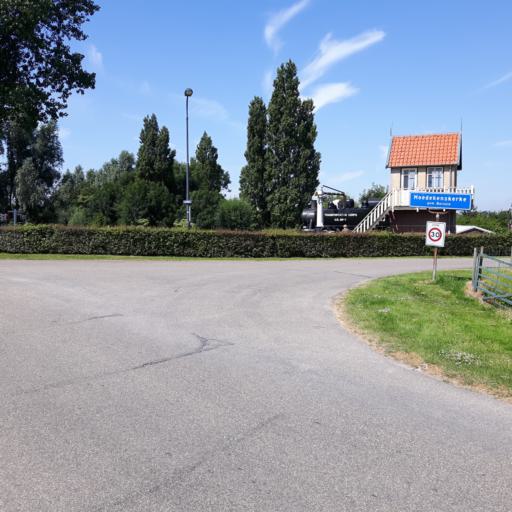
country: NL
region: Zeeland
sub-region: Gemeente Goes
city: Goes
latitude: 51.4215
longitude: 3.9150
